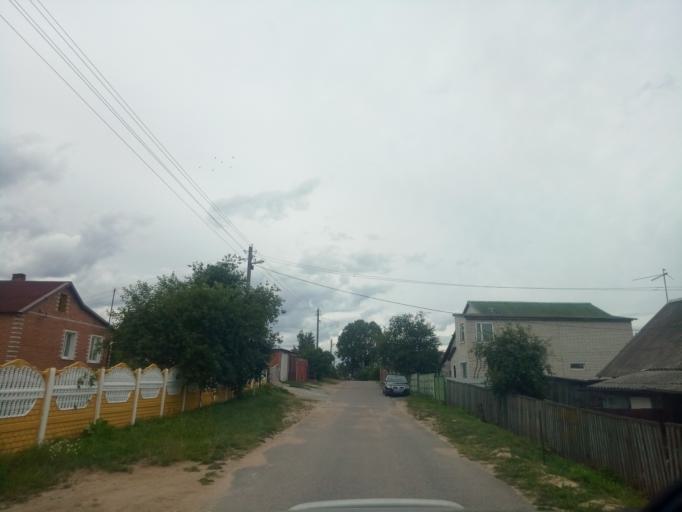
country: BY
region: Minsk
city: Zhdanovichy
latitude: 53.9174
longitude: 27.3917
